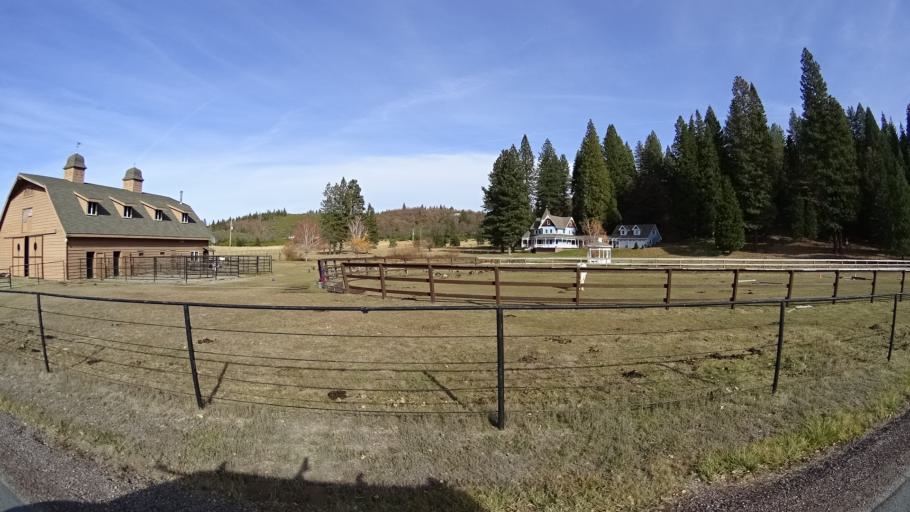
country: US
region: California
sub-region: Siskiyou County
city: Weed
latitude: 41.4007
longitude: -122.4214
